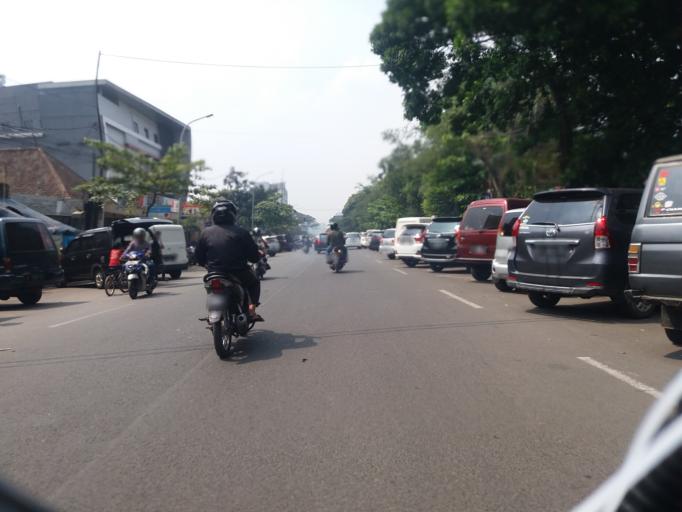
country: ID
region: West Java
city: Bandung
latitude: -6.9165
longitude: 107.5918
